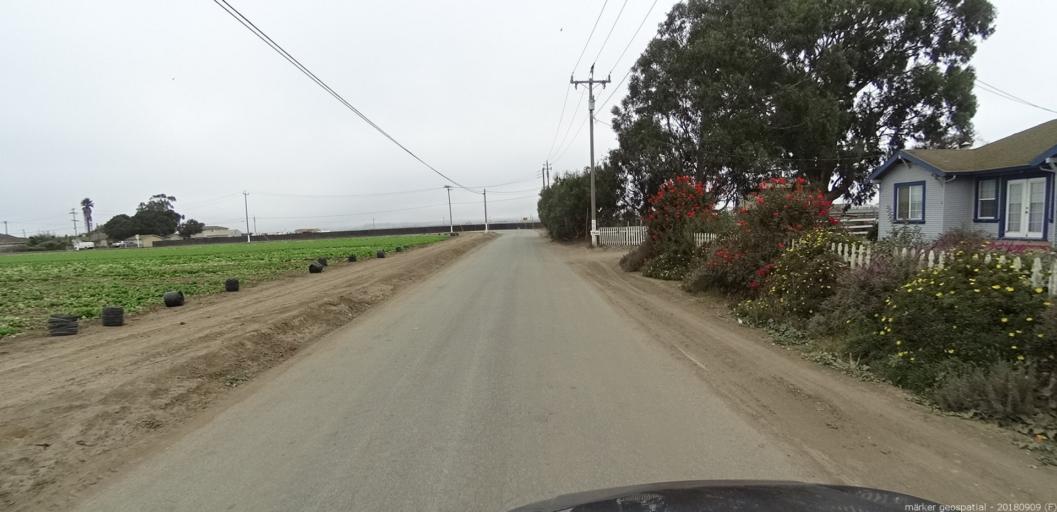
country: US
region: California
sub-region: Monterey County
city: Boronda
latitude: 36.7124
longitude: -121.6753
